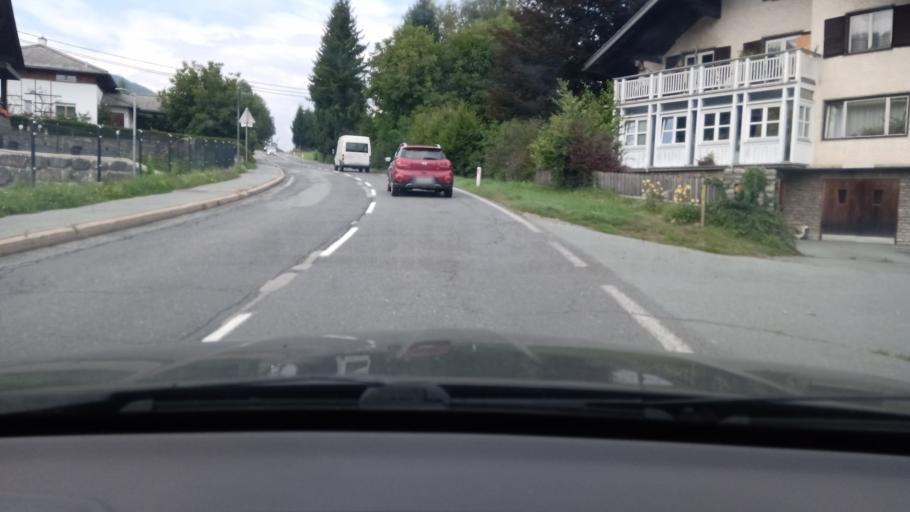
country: AT
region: Carinthia
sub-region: Politischer Bezirk Hermagor
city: Hermagor
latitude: 46.6284
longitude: 13.3619
